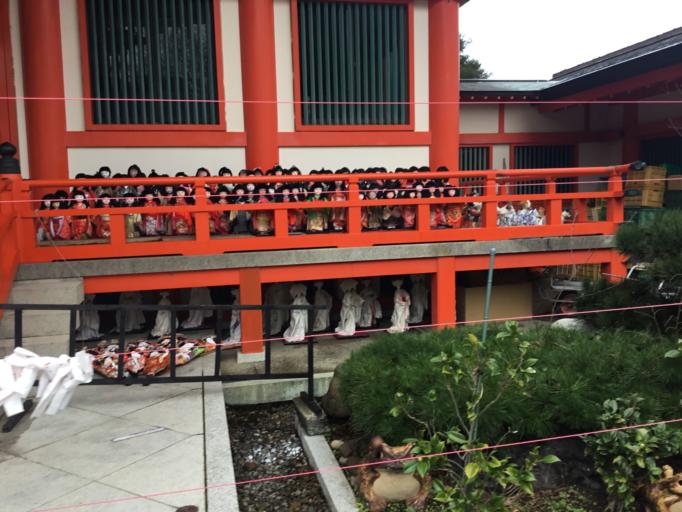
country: JP
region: Wakayama
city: Minato
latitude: 34.2738
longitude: 135.0665
